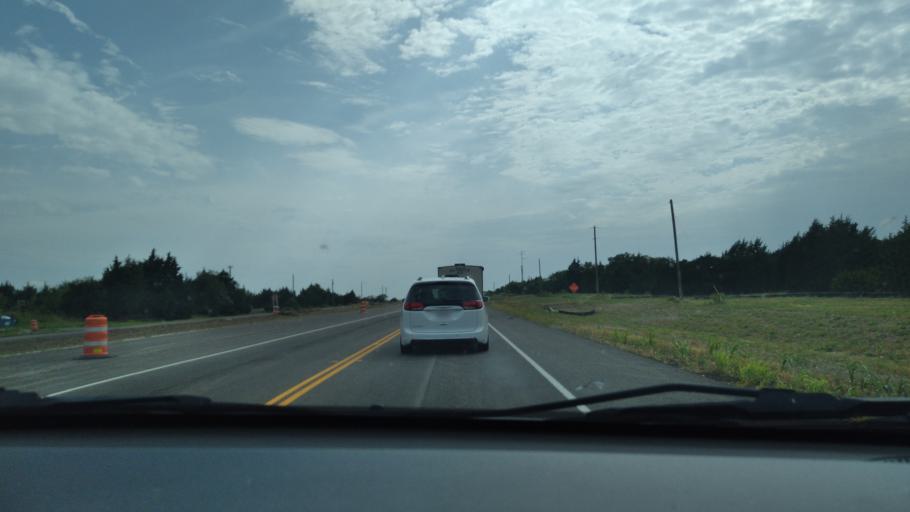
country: US
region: Texas
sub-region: Hill County
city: Hubbard
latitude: 31.8740
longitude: -96.7616
